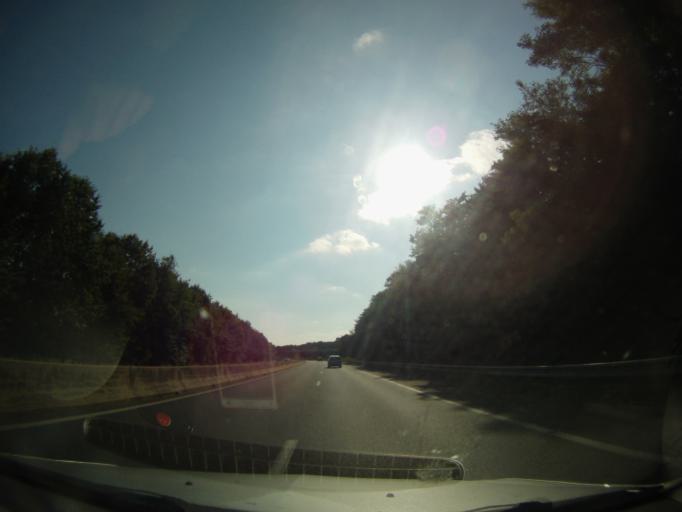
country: FR
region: Pays de la Loire
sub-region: Departement de la Loire-Atlantique
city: Carquefou
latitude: 47.2916
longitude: -1.4960
